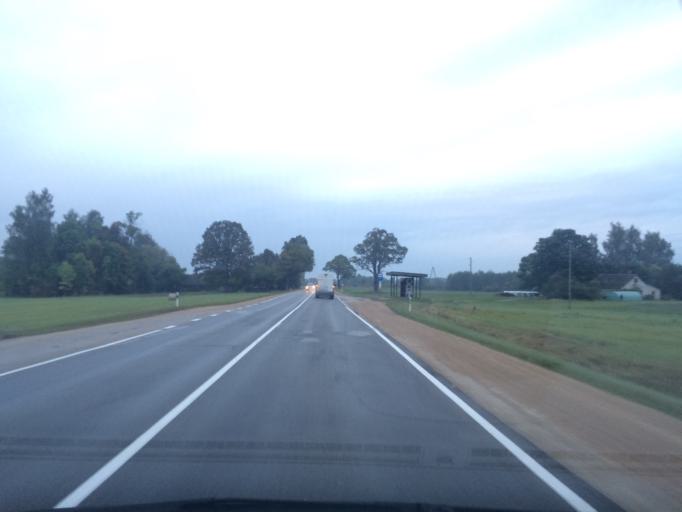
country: LV
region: Plavinu
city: Plavinas
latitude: 56.5794
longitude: 25.7774
